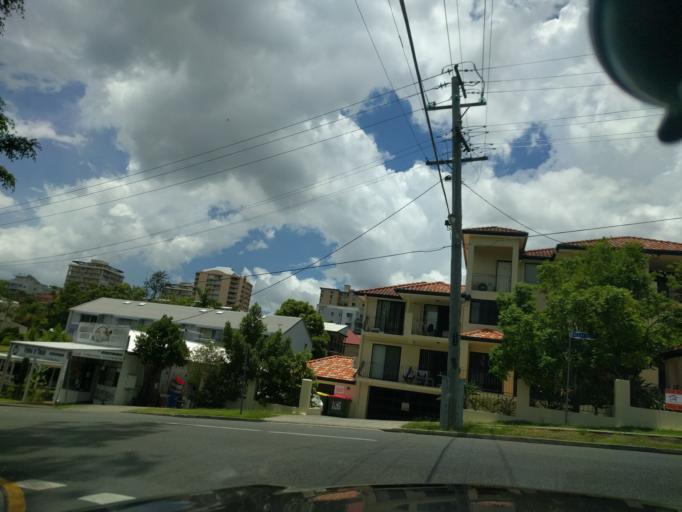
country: AU
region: Queensland
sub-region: Brisbane
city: Milton
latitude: -27.4752
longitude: 152.9982
